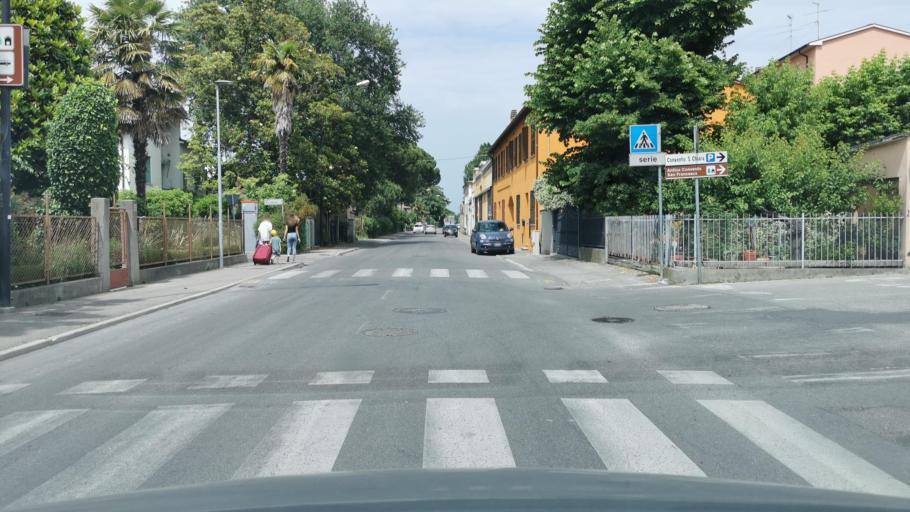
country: IT
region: Emilia-Romagna
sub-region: Provincia di Ravenna
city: Bagnacavallo
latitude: 44.4166
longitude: 11.9726
